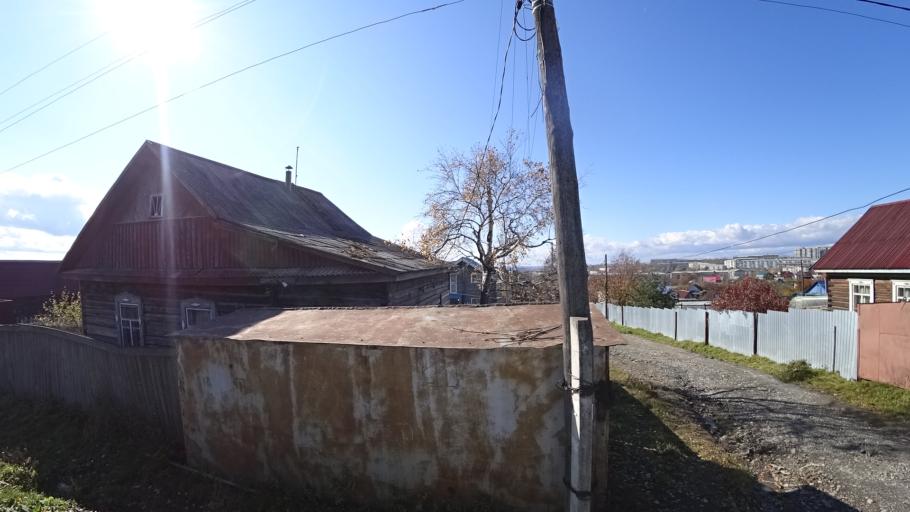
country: RU
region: Khabarovsk Krai
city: Amursk
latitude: 50.2370
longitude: 136.9187
